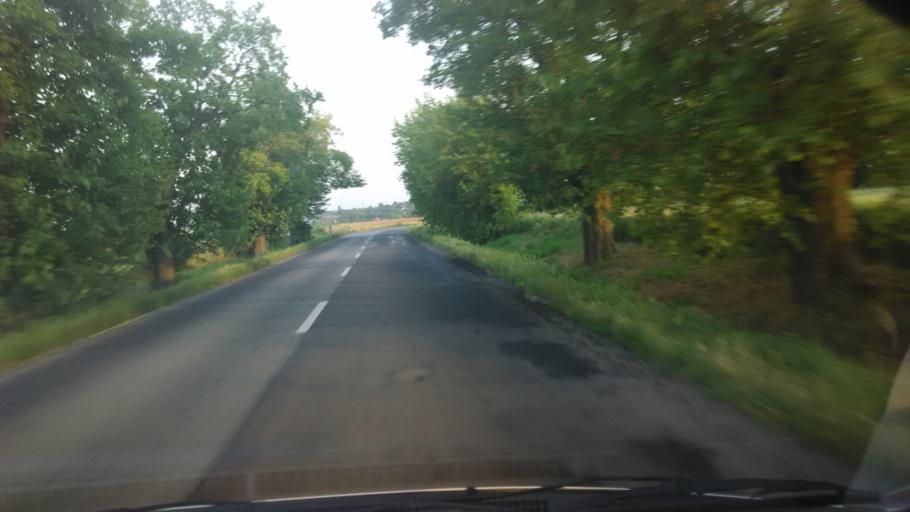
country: SK
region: Nitriansky
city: Tlmace
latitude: 48.1646
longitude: 18.4518
